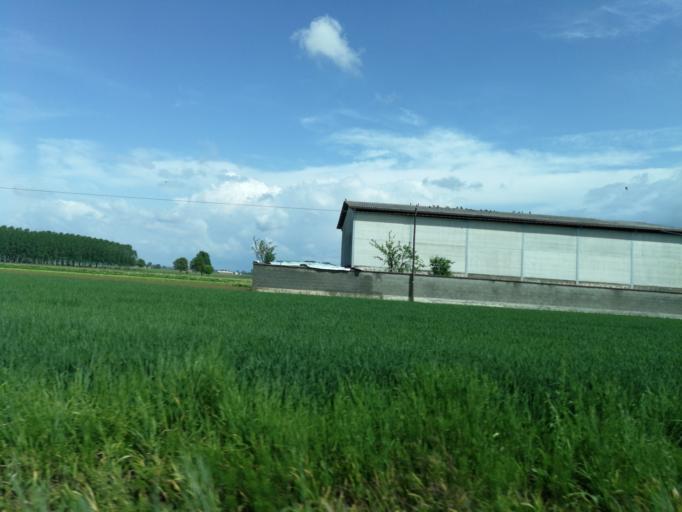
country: IT
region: Piedmont
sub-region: Provincia di Cuneo
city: Moretta
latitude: 44.7707
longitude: 7.5458
